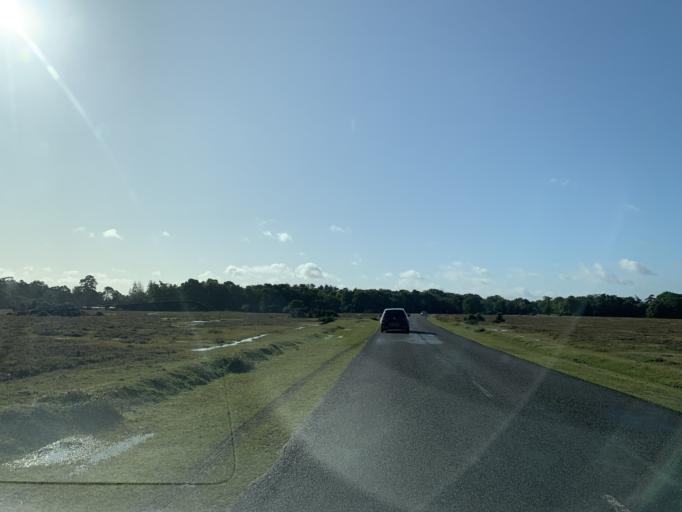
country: GB
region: England
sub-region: Wiltshire
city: Whiteparish
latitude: 50.9349
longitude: -1.6544
